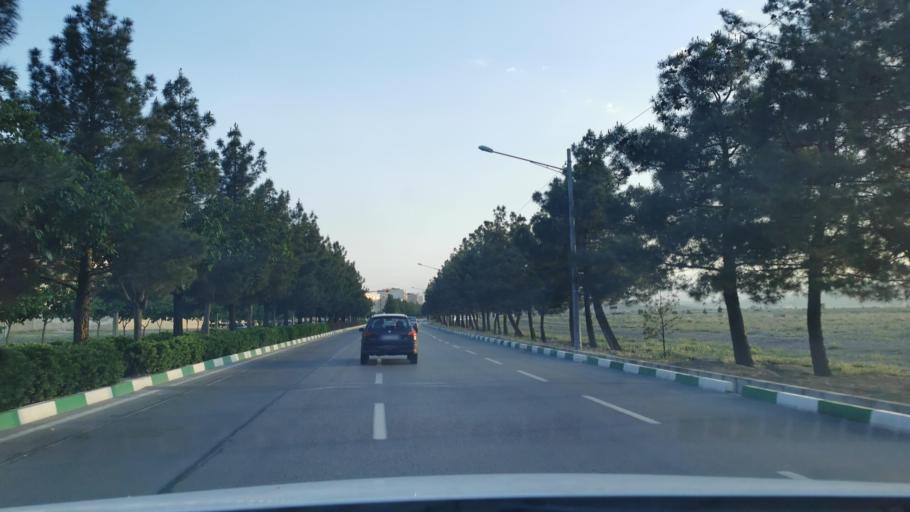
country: IR
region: Razavi Khorasan
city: Torqabeh
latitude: 36.3823
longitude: 59.4623
